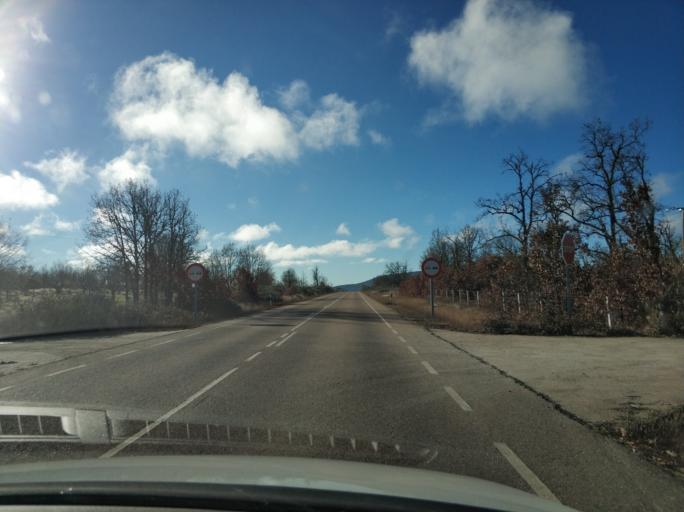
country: ES
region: Castille and Leon
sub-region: Provincia de Salamanca
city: Herguijuela del Campo
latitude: 40.6287
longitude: -5.9059
